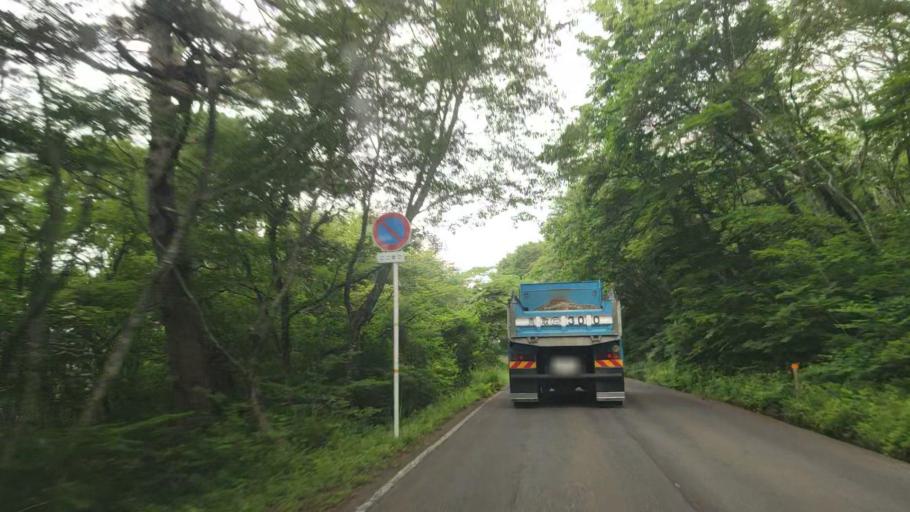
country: JP
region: Tottori
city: Yonago
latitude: 35.3737
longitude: 133.5177
